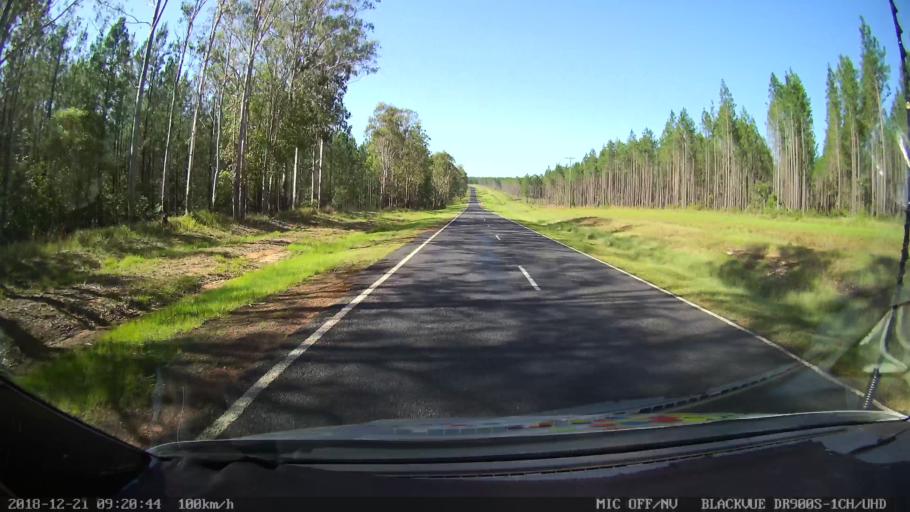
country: AU
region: New South Wales
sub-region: Clarence Valley
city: Maclean
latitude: -29.3188
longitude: 152.9999
